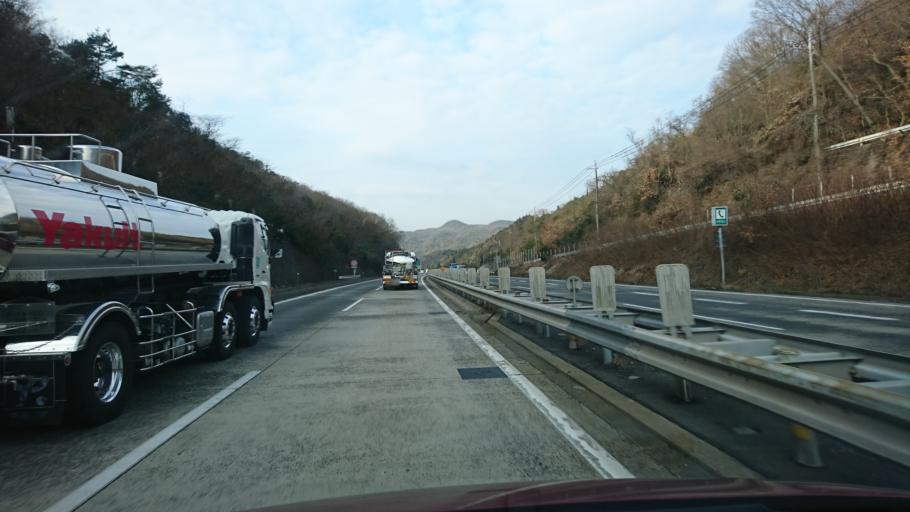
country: JP
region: Hyogo
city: Kariya
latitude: 34.7836
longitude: 134.2723
